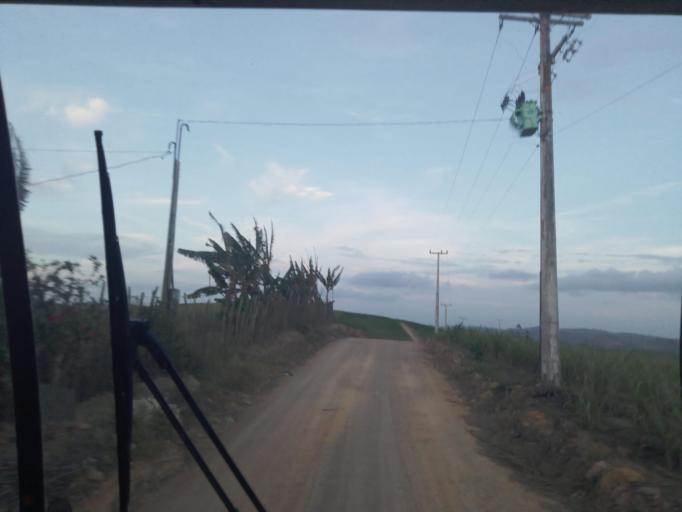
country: BR
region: Pernambuco
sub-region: Vitoria De Santo Antao
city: Vitoria de Santo Antao
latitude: -8.1565
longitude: -35.2522
